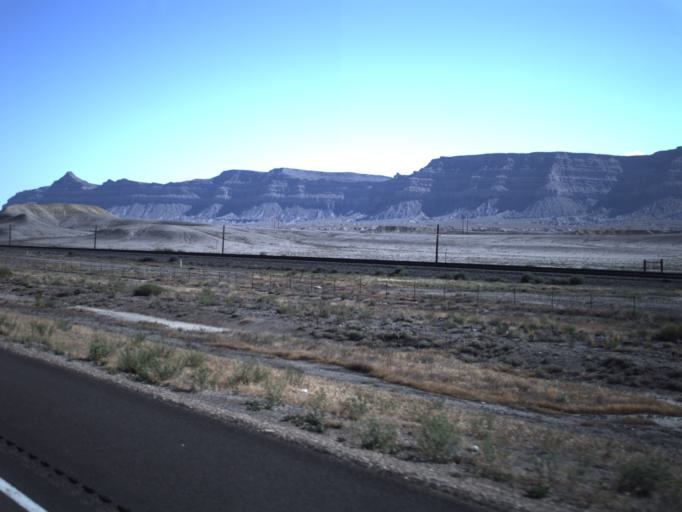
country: US
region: Utah
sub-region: Carbon County
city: East Carbon City
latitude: 39.0888
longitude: -110.3200
